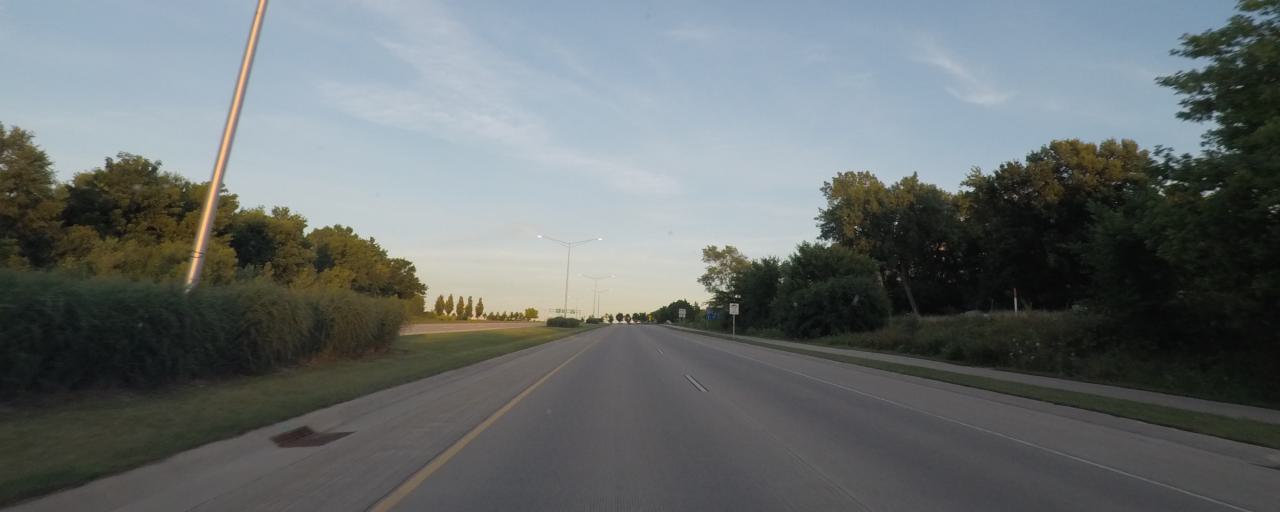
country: US
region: Wisconsin
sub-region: Rock County
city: Janesville
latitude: 42.6732
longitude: -88.9901
